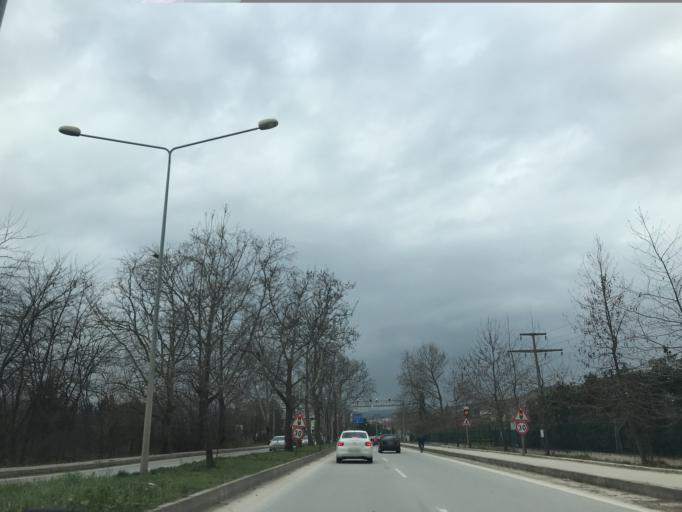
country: TR
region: Yalova
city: Kadikoy
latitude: 40.6470
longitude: 29.2354
